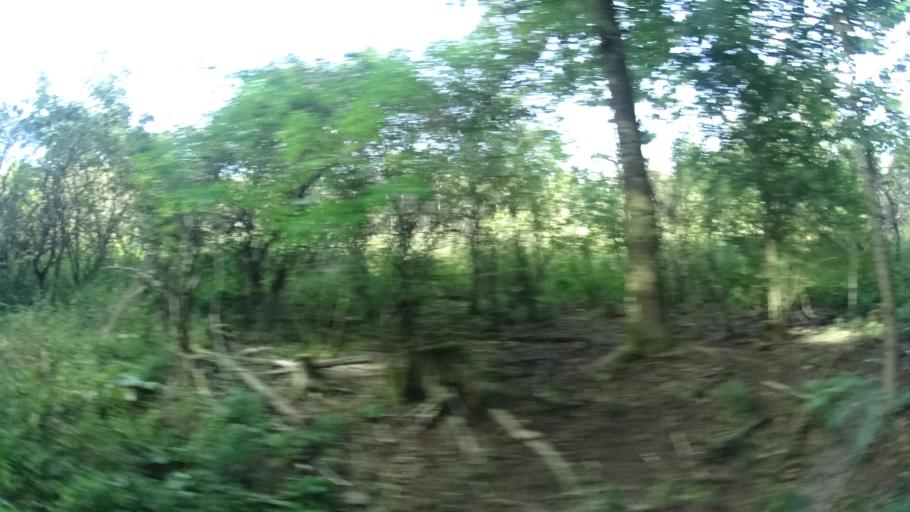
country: DE
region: Bavaria
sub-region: Regierungsbezirk Unterfranken
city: Hausen
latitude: 50.4986
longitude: 10.1011
